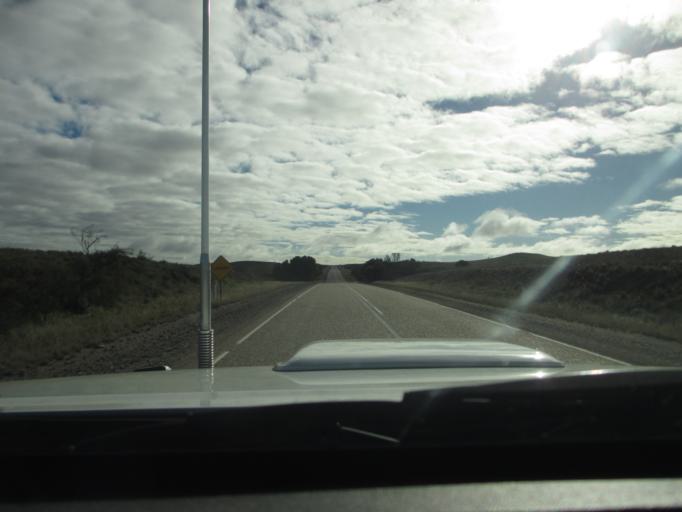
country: AU
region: South Australia
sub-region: Peterborough
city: Peterborough
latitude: -32.5744
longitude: 138.5629
